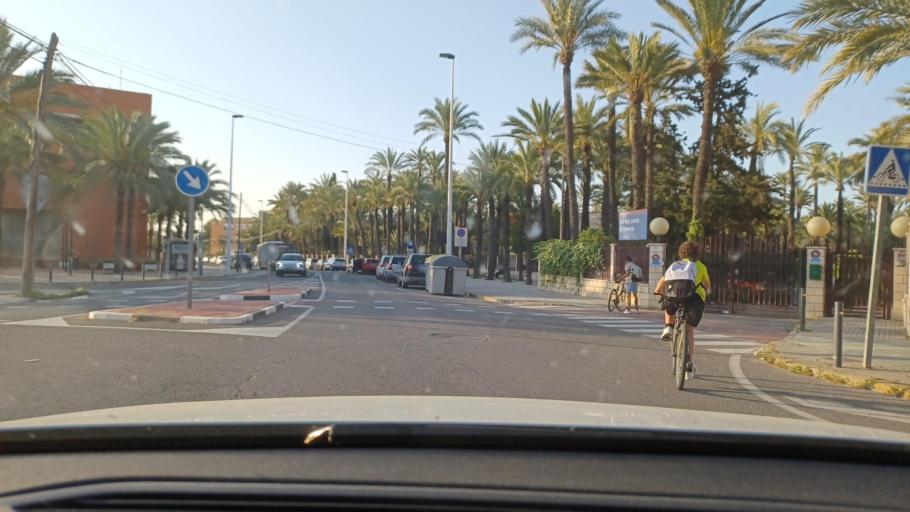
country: ES
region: Valencia
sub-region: Provincia de Alicante
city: Elche
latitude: 38.2630
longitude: -0.6886
